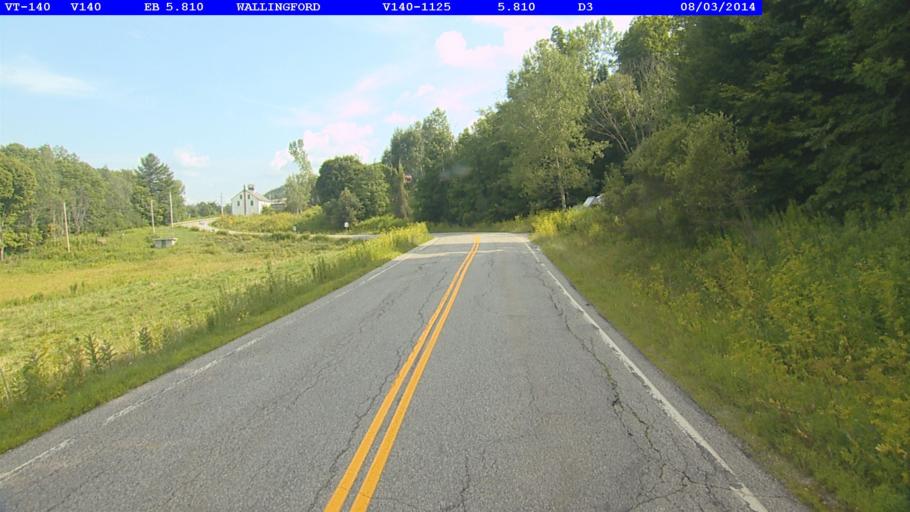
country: US
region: Vermont
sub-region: Rutland County
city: Rutland
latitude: 43.4526
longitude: -72.8801
